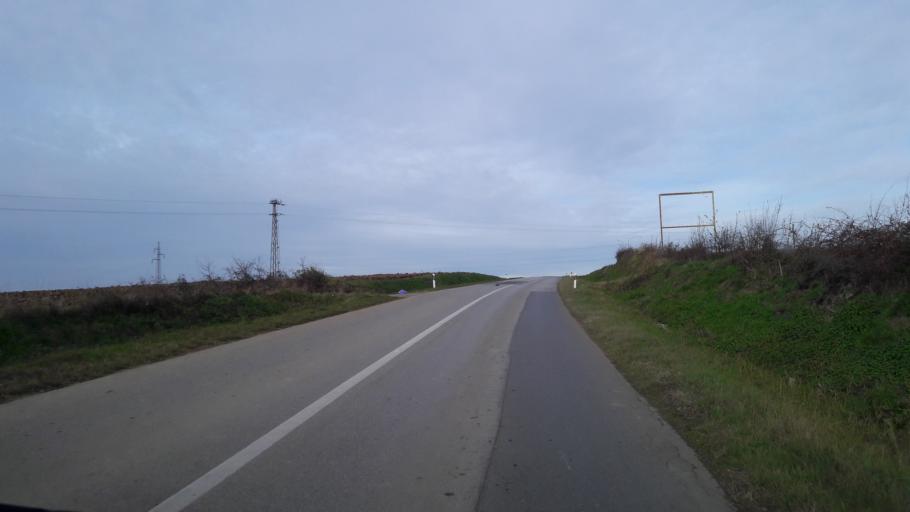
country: HR
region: Osjecko-Baranjska
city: Piskorevci
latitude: 45.2867
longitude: 18.4337
